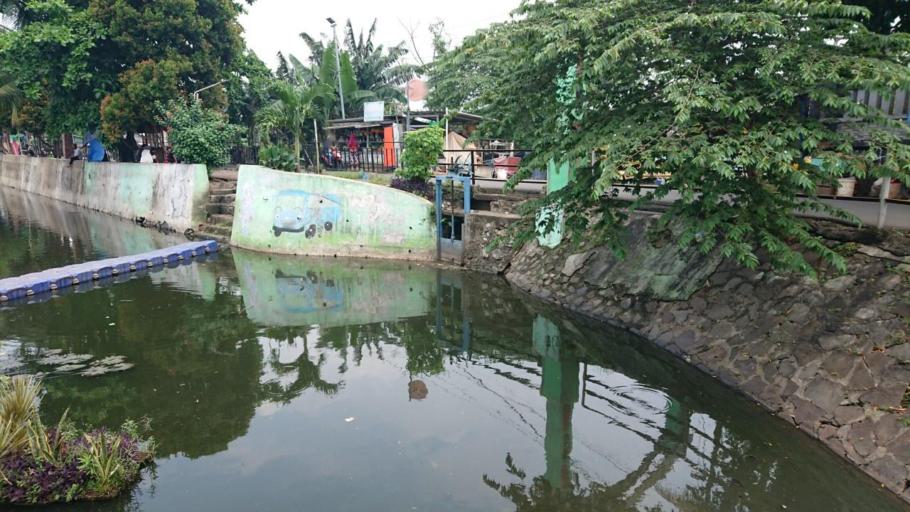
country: ID
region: West Java
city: Depok
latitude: -6.3471
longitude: 106.8567
